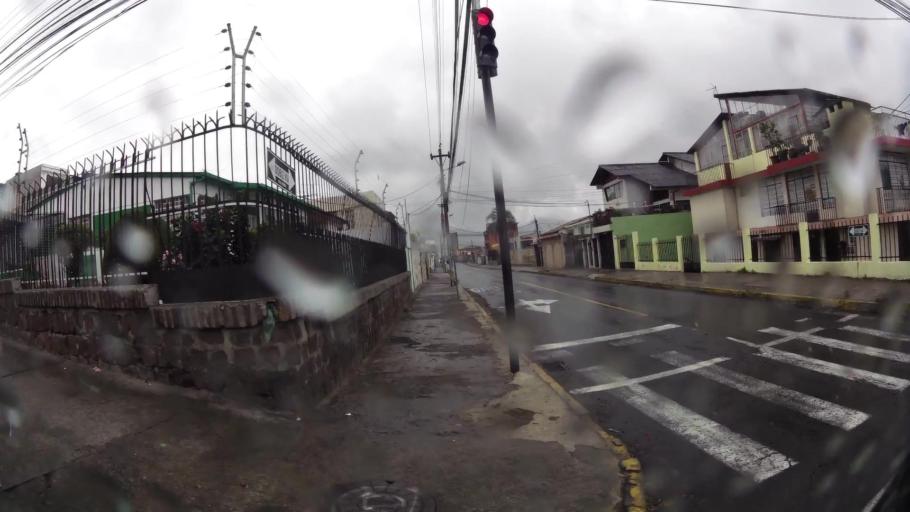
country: EC
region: Pichincha
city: Quito
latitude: -0.1237
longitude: -78.4967
